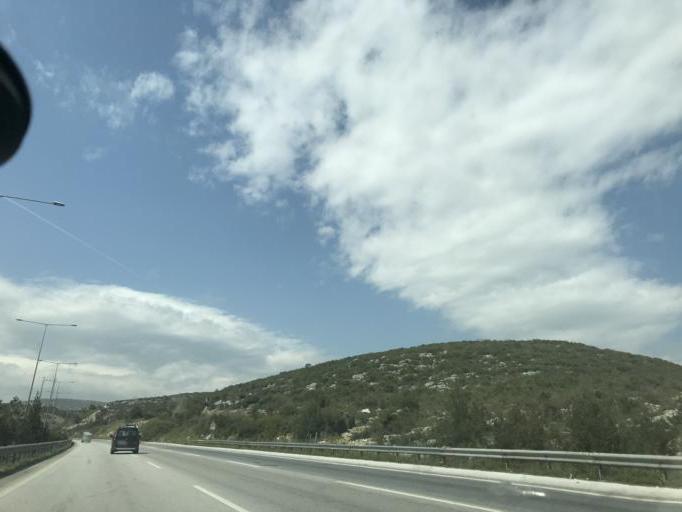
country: TR
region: Mersin
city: Tarsus
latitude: 37.1458
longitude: 34.8419
